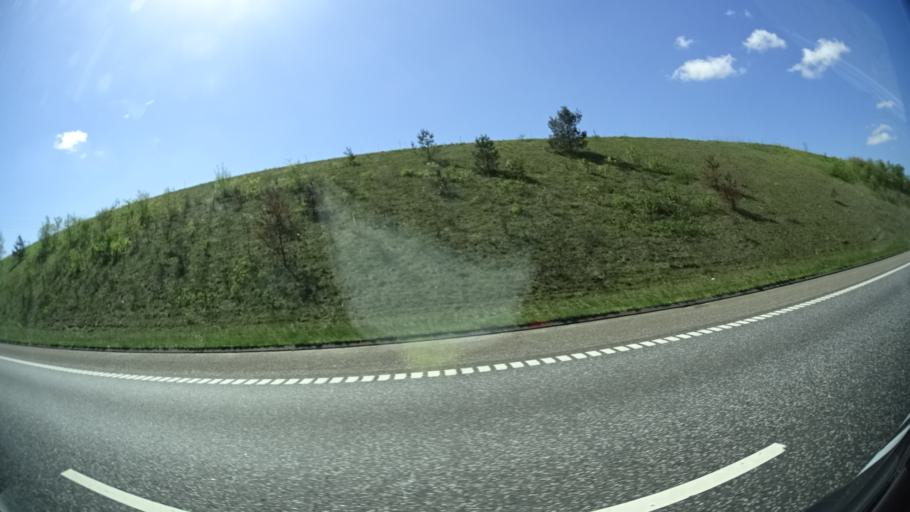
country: DK
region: Central Jutland
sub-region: Randers Kommune
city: Assentoft
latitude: 56.3841
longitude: 10.1115
